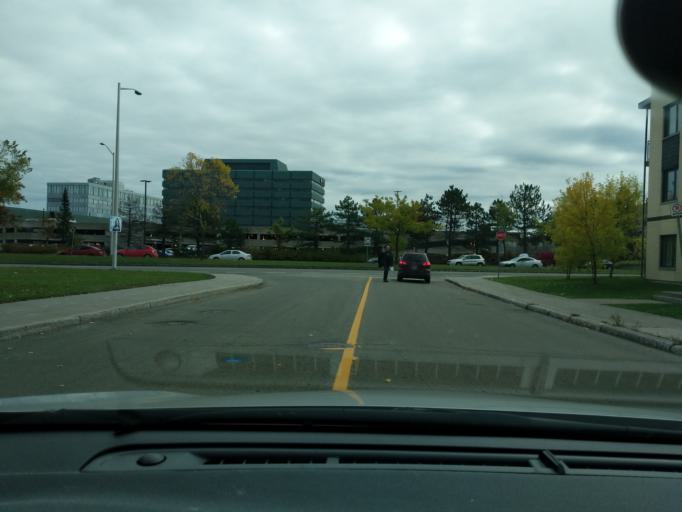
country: CA
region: Quebec
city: L'Ancienne-Lorette
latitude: 46.7714
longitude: -71.2890
